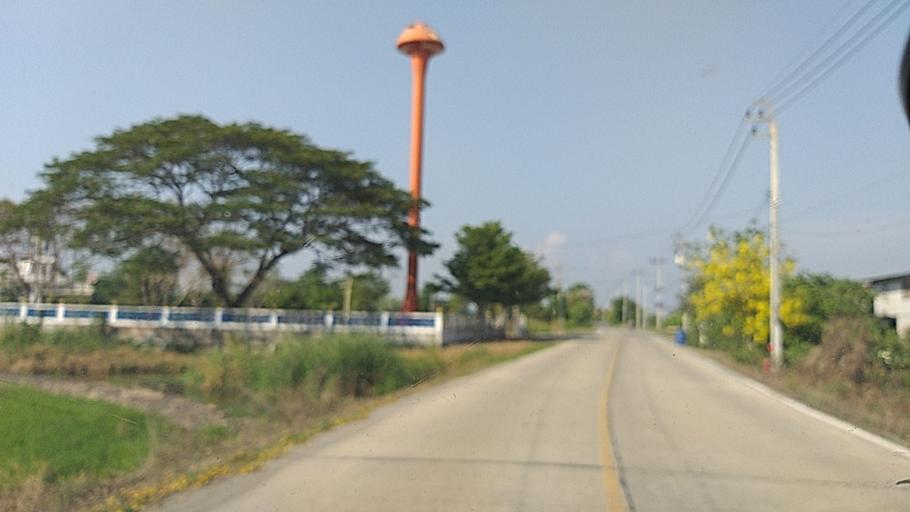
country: TH
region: Nonthaburi
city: Sai Noi
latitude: 13.9359
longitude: 100.3217
